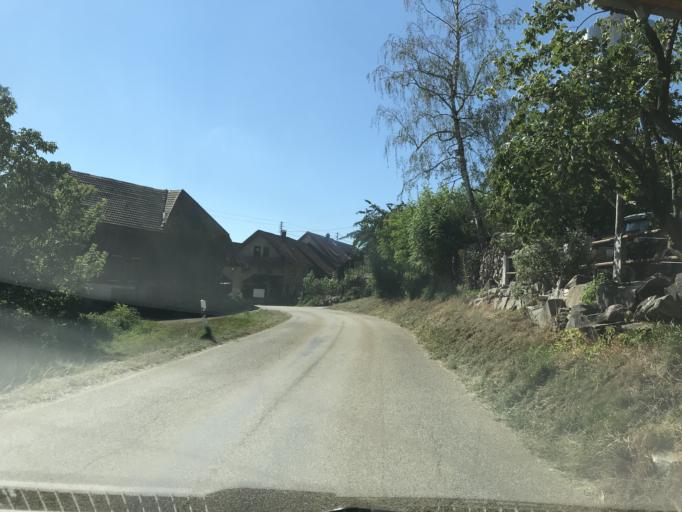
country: DE
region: Baden-Wuerttemberg
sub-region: Freiburg Region
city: Hasel
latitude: 47.6649
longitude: 7.8702
